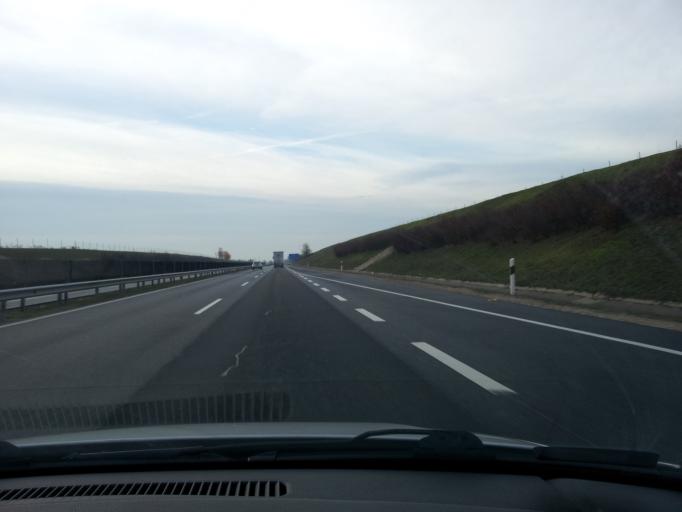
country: HU
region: Fejer
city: Rackeresztur
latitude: 47.3047
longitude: 18.8670
